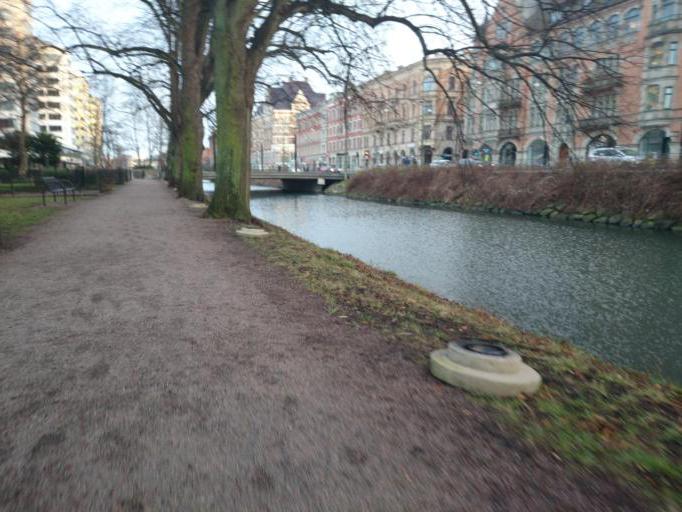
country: SE
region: Skane
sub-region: Malmo
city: Malmoe
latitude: 55.6010
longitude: 12.9981
